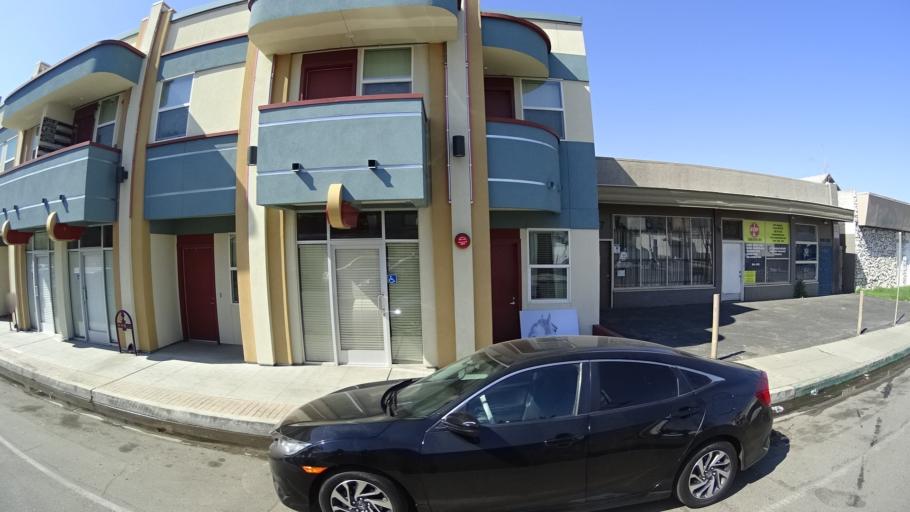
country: US
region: California
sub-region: Fresno County
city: Fresno
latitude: 36.7520
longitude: -119.8004
